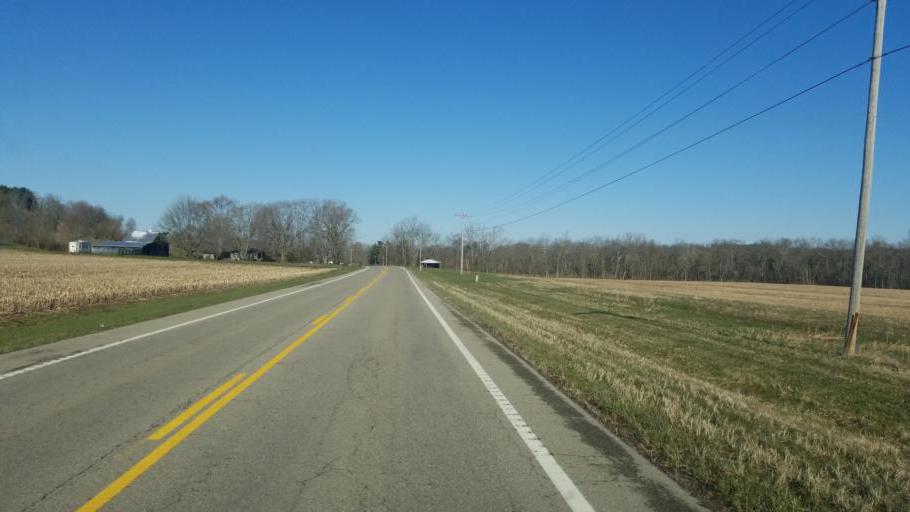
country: US
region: Ohio
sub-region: Highland County
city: Greenfield
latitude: 39.2285
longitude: -83.3209
